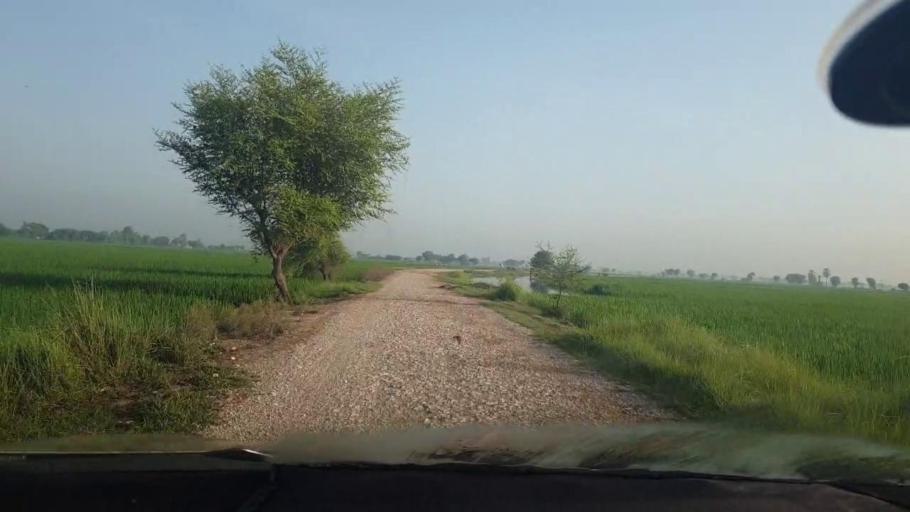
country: PK
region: Sindh
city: Kambar
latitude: 27.6242
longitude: 68.0176
